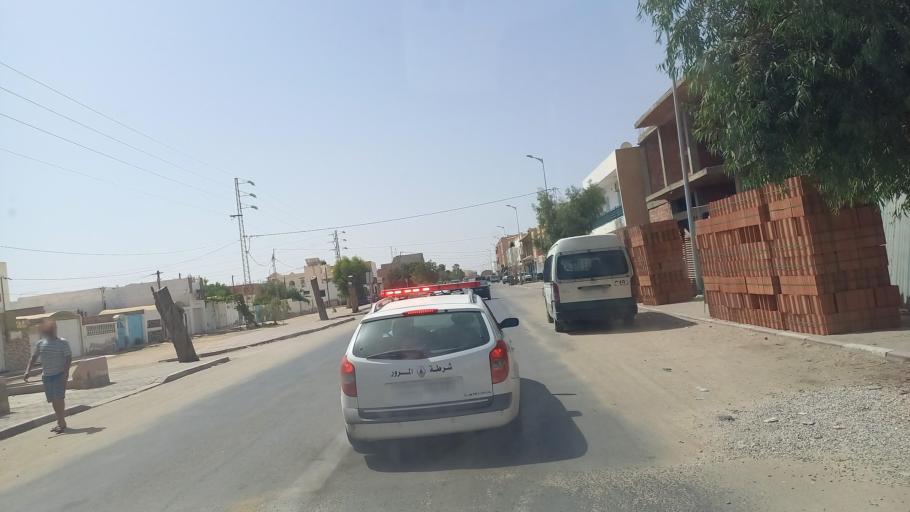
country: TN
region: Madanin
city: Medenine
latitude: 33.3268
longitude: 10.4846
